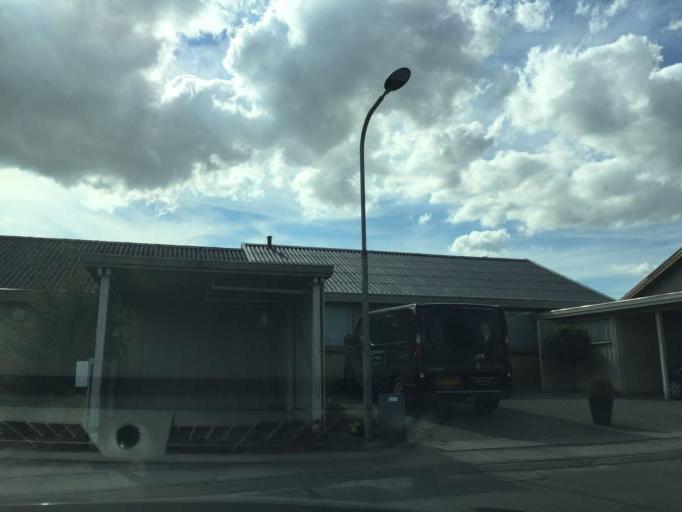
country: DK
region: South Denmark
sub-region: Odense Kommune
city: Odense
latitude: 55.3469
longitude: 10.3849
